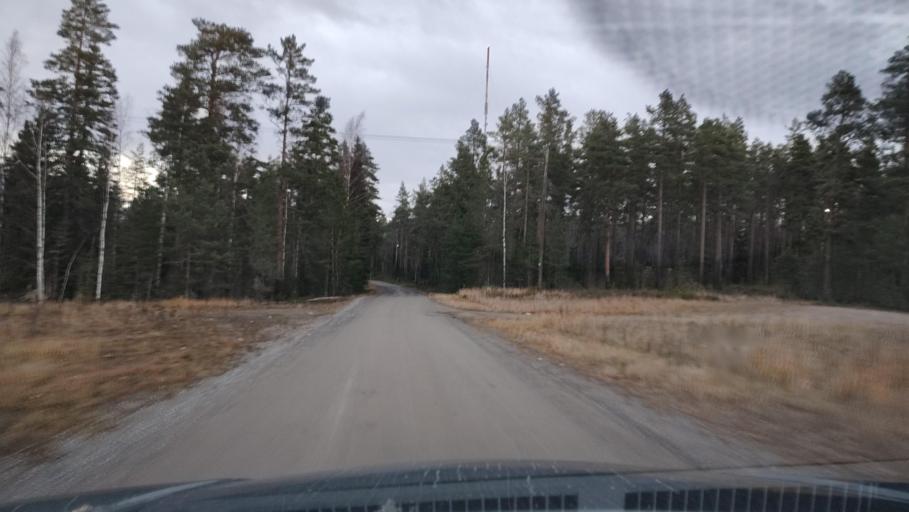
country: FI
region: Southern Ostrobothnia
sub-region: Suupohja
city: Karijoki
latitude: 62.2834
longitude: 21.6315
